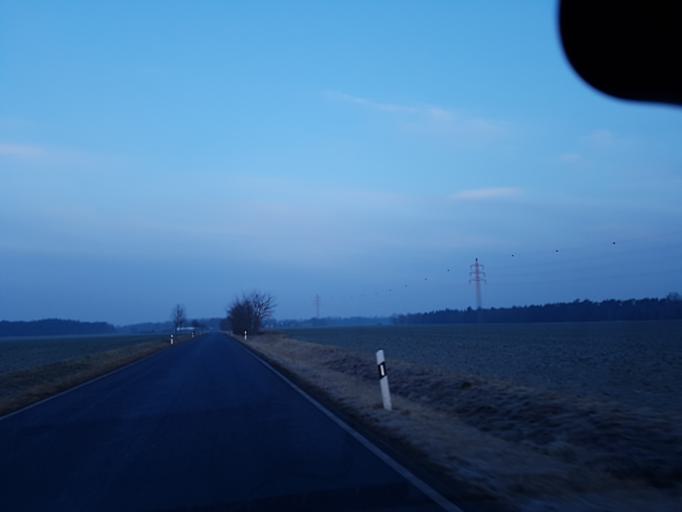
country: DE
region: Saxony-Anhalt
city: Holzdorf
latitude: 51.7647
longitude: 13.0992
